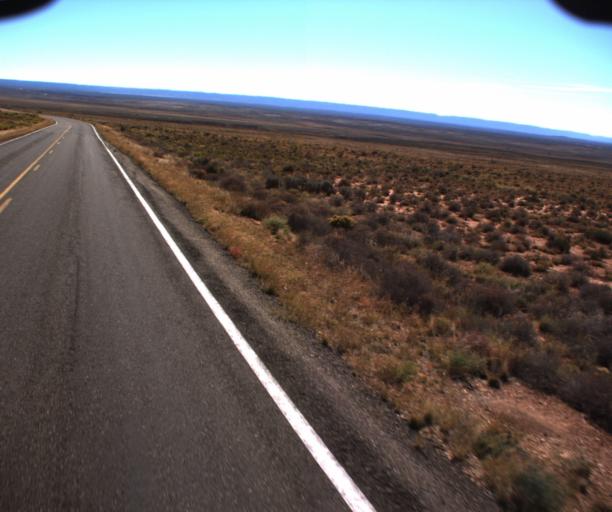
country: US
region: Arizona
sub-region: Coconino County
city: Fredonia
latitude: 36.9295
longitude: -112.4896
